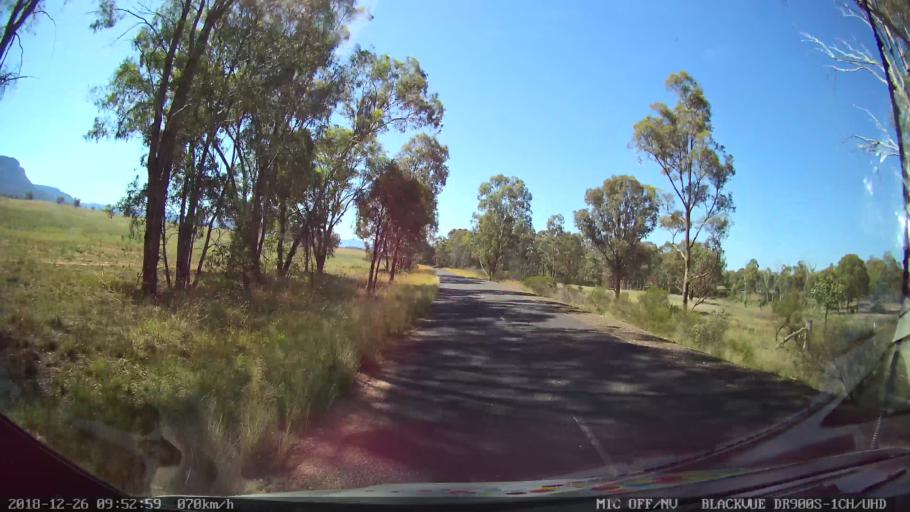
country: AU
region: New South Wales
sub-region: Mid-Western Regional
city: Kandos
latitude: -33.0162
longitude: 150.1511
